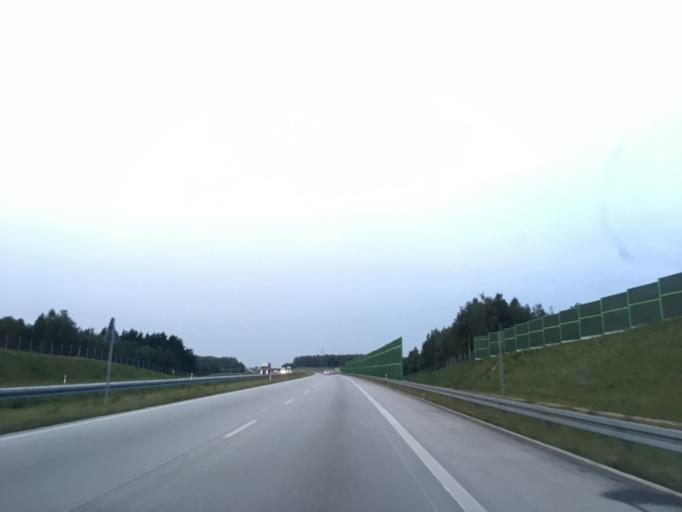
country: PL
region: Lodz Voivodeship
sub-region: Powiat lodzki wschodni
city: Andrespol
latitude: 51.7766
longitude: 19.6048
